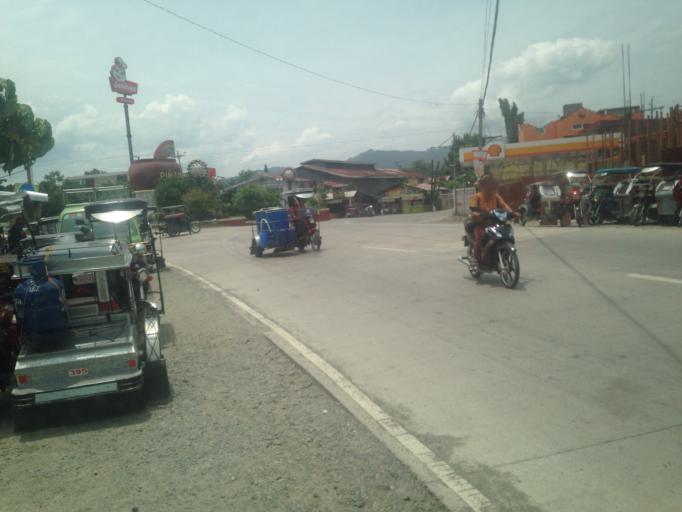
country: PH
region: Mimaropa
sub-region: Province of Mindoro Oriental
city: Pinamalayan
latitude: 13.0381
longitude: 121.4801
